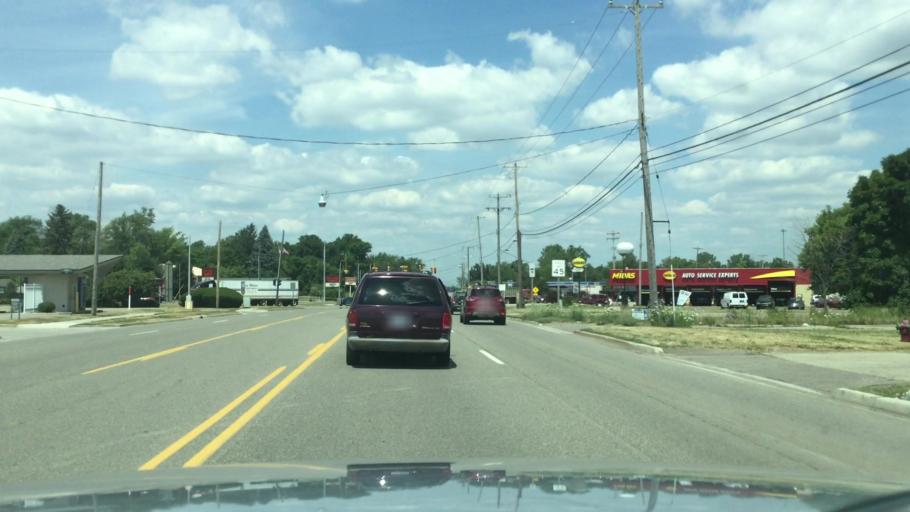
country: US
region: Michigan
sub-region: Genesee County
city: Grand Blanc
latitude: 42.9453
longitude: -83.6514
